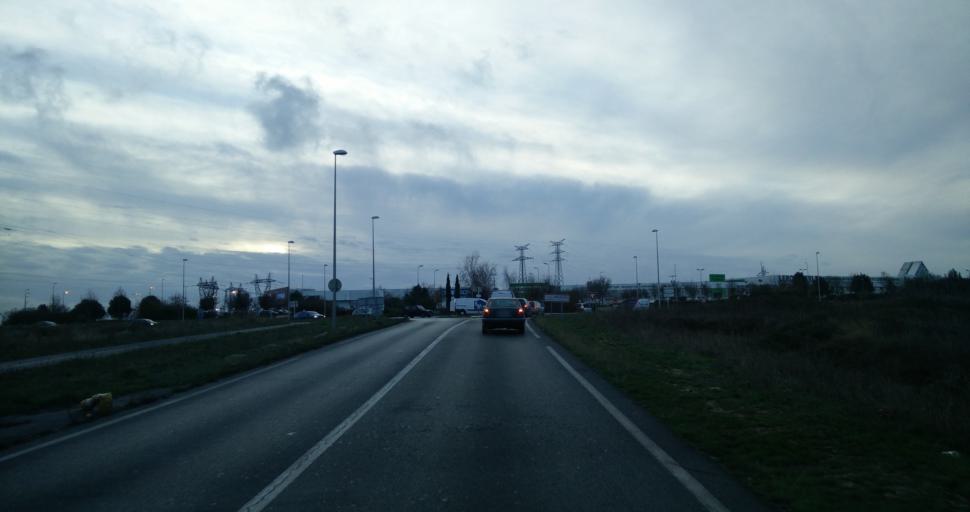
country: FR
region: Poitou-Charentes
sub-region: Departement de la Charente-Maritime
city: Puilboreau
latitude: 46.1799
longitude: -1.1239
